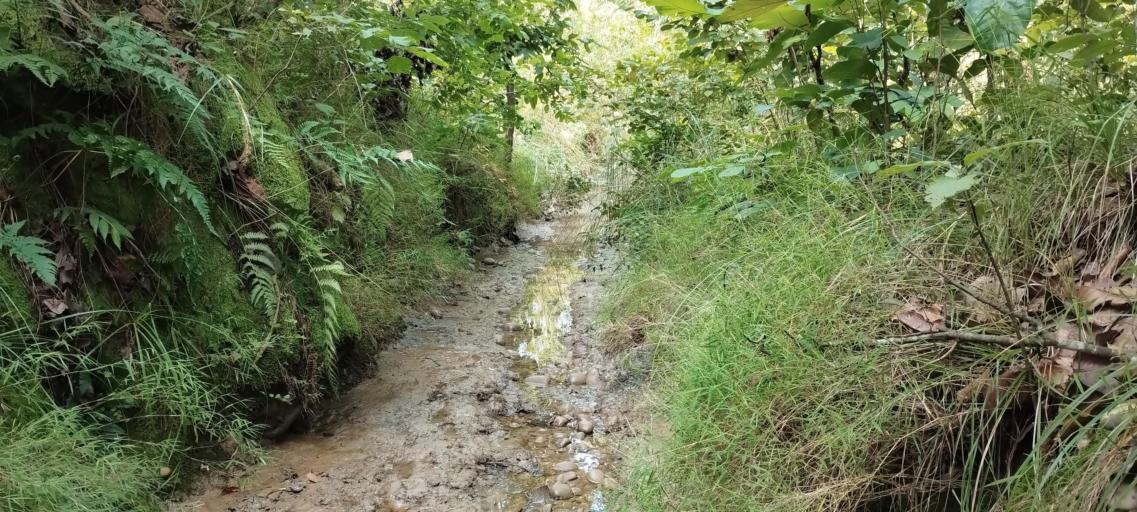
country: NP
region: Far Western
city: Tikapur
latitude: 28.4766
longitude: 81.2524
